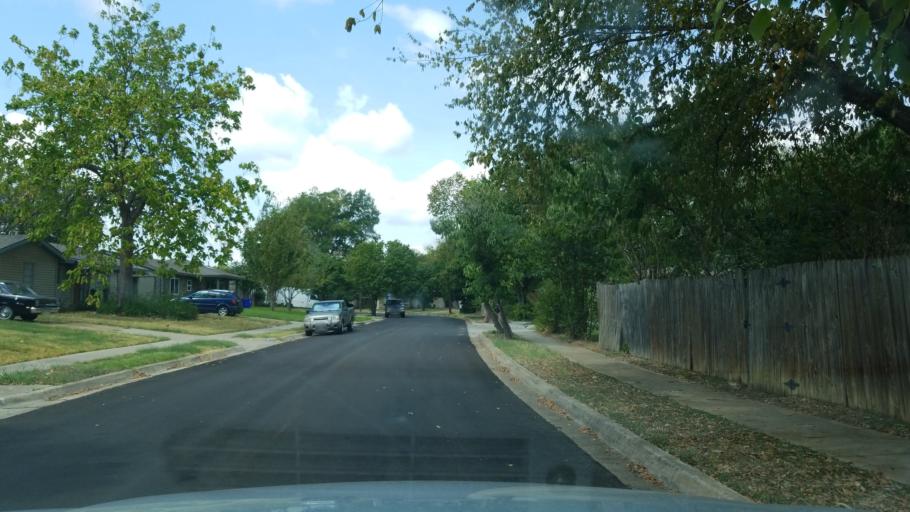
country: US
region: Texas
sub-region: Tarrant County
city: Euless
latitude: 32.8490
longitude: -97.0863
